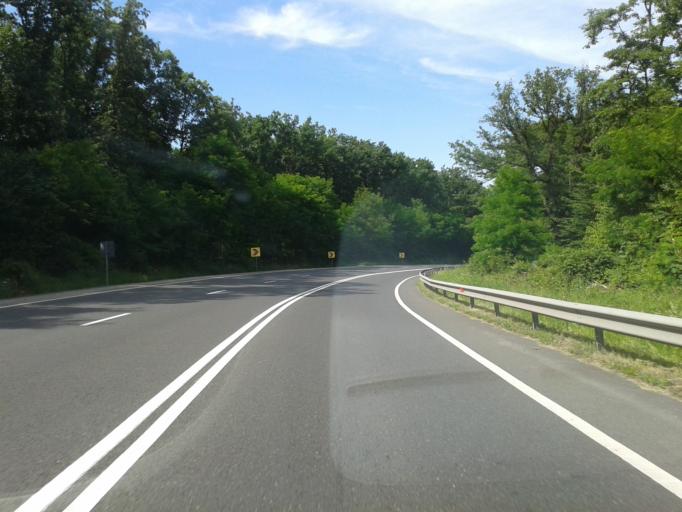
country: RO
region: Hunedoara
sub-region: Comuna Santamaria-Orlea
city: Santamaria-Orlea
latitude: 45.6199
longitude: 22.9857
